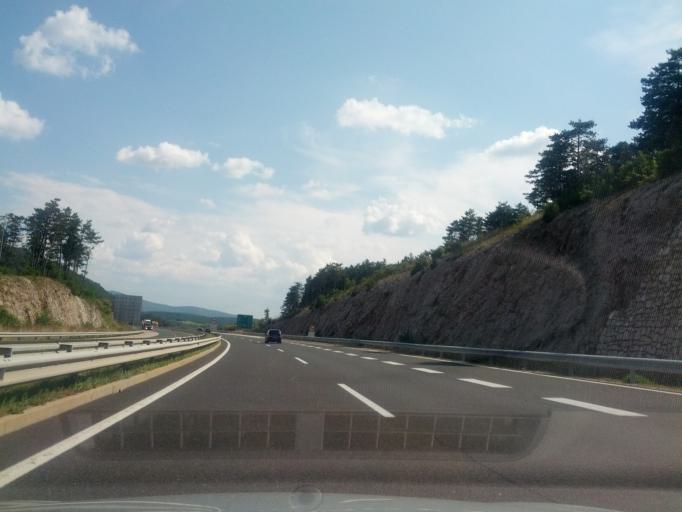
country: SI
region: Hrpelje-Kozina
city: Kozina
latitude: 45.6049
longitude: 13.9275
